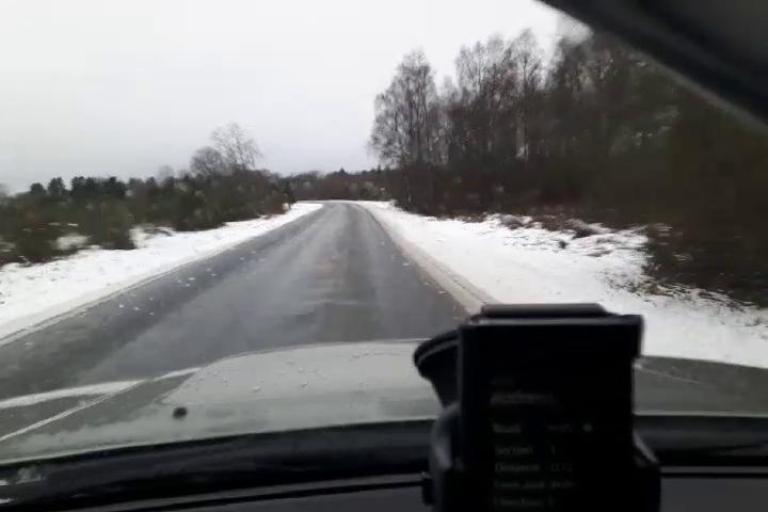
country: EE
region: Harju
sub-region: Harku vald
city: Tabasalu
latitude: 59.4281
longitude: 24.4309
